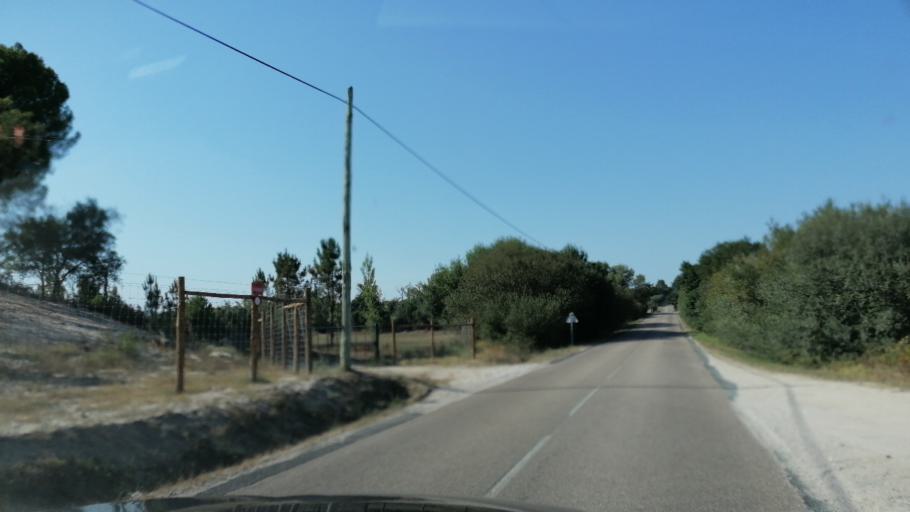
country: PT
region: Evora
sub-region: Vendas Novas
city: Vendas Novas
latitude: 38.7953
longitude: -8.5786
